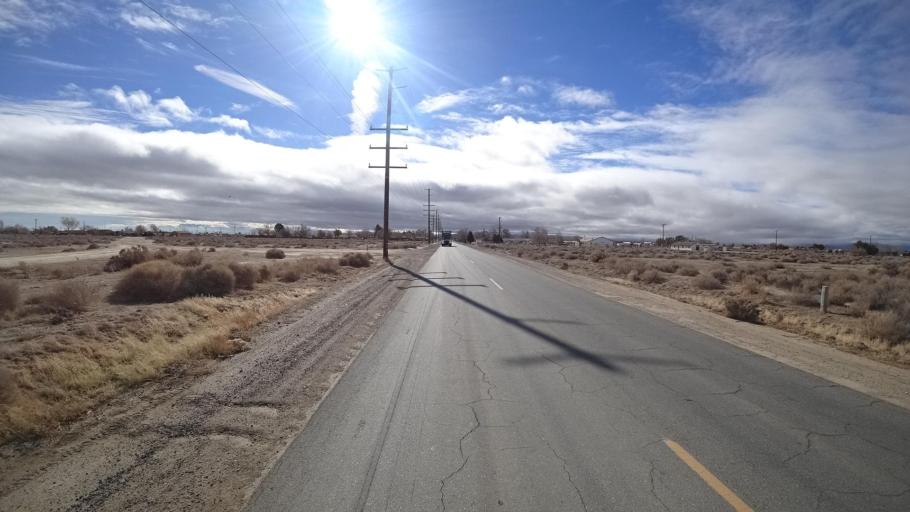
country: US
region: California
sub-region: Kern County
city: Rosamond
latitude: 34.8535
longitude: -118.2379
